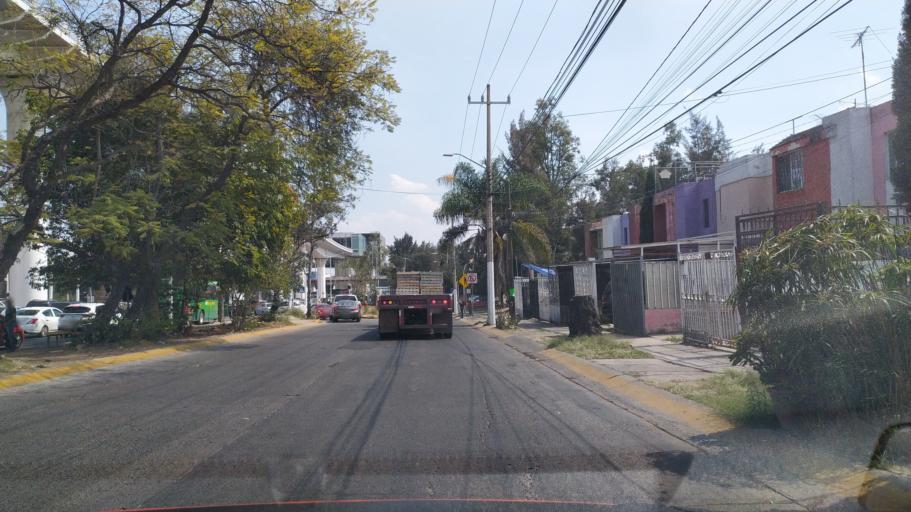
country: MX
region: Jalisco
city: Zapopan2
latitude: 20.7404
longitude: -103.4072
